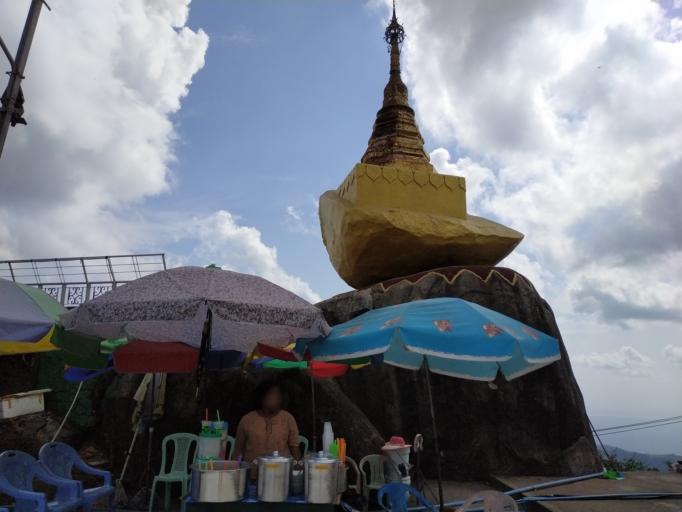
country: MM
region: Mon
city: Kyaikto
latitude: 17.4792
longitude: 97.1002
